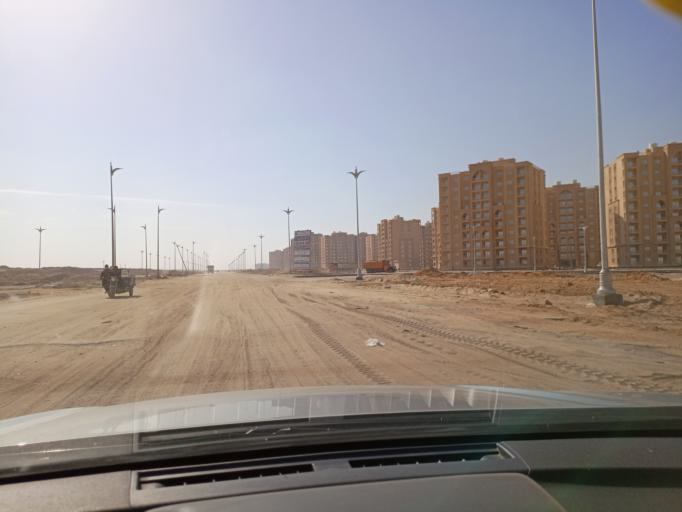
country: EG
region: Muhafazat al Qalyubiyah
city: Al Khankah
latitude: 30.0228
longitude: 31.6621
